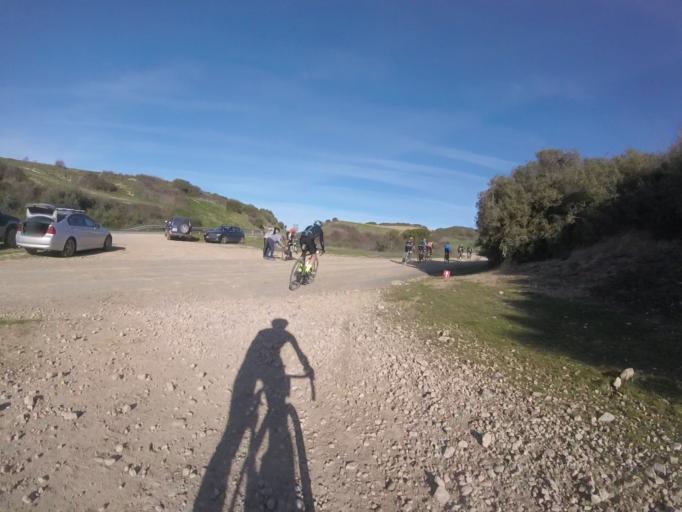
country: ES
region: Navarre
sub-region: Provincia de Navarra
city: Yerri
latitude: 42.7006
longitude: -1.9663
